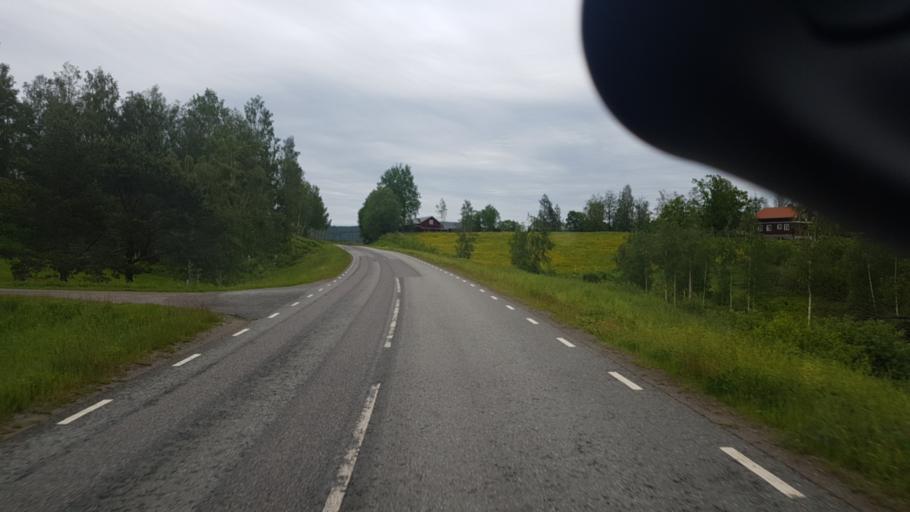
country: SE
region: Vaermland
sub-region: Eda Kommun
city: Amotfors
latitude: 59.6843
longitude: 12.1049
